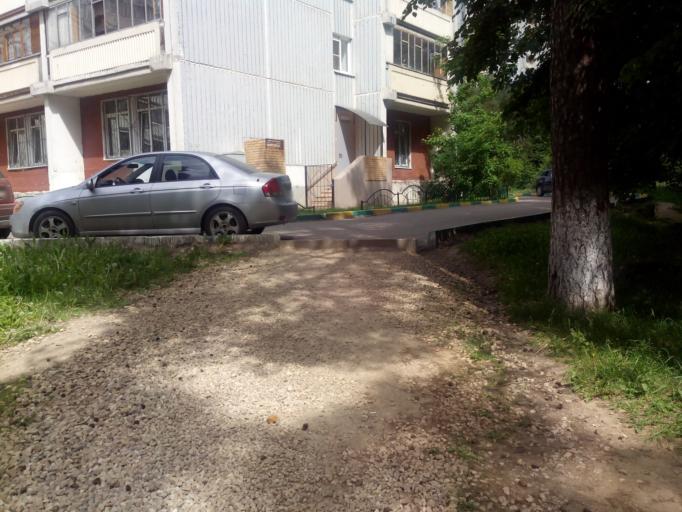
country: RU
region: Moskovskaya
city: Odintsovo
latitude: 55.6658
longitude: 37.2941
